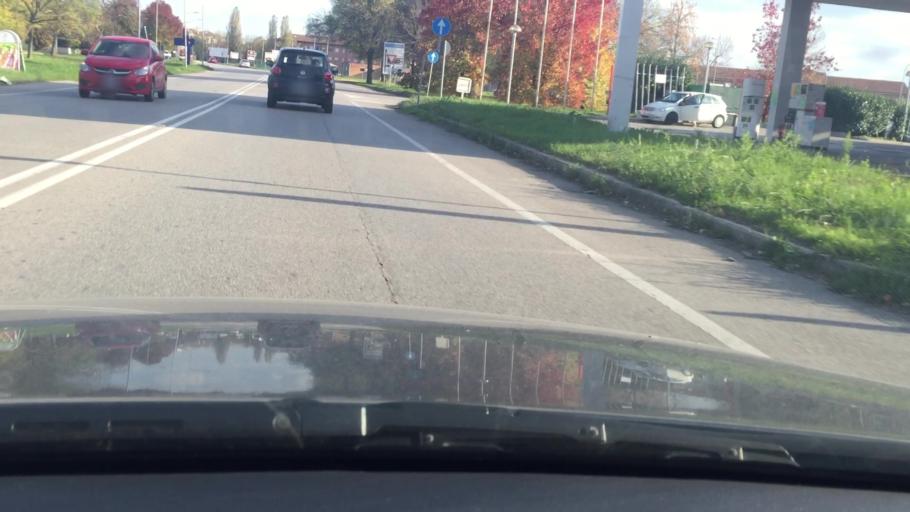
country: IT
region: Emilia-Romagna
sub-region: Provincia di Ferrara
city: Ferrara
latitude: 44.8173
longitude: 11.6078
